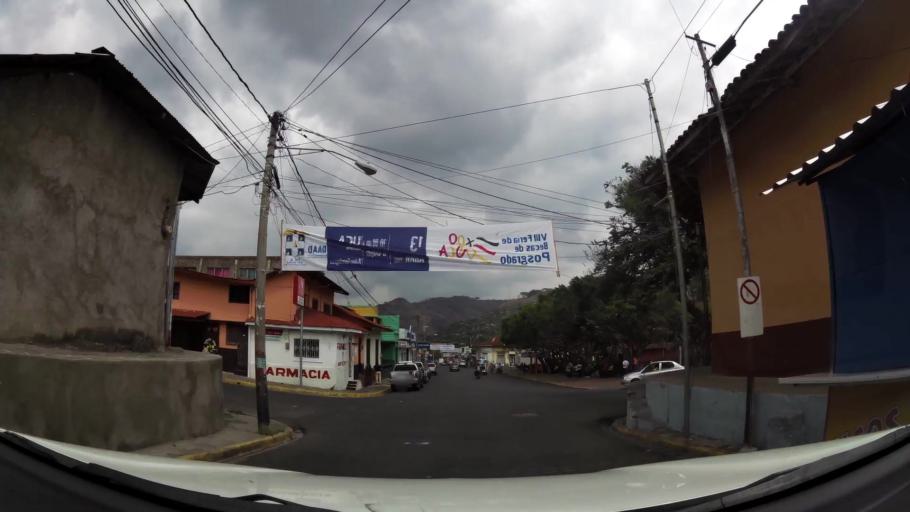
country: NI
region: Matagalpa
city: Matagalpa
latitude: 12.9212
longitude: -85.9194
